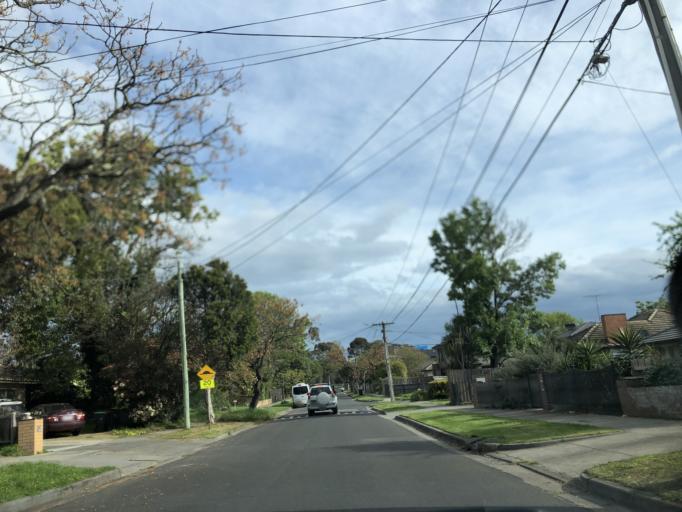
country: AU
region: Victoria
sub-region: Monash
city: Oakleigh South
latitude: -37.9255
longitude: 145.0861
